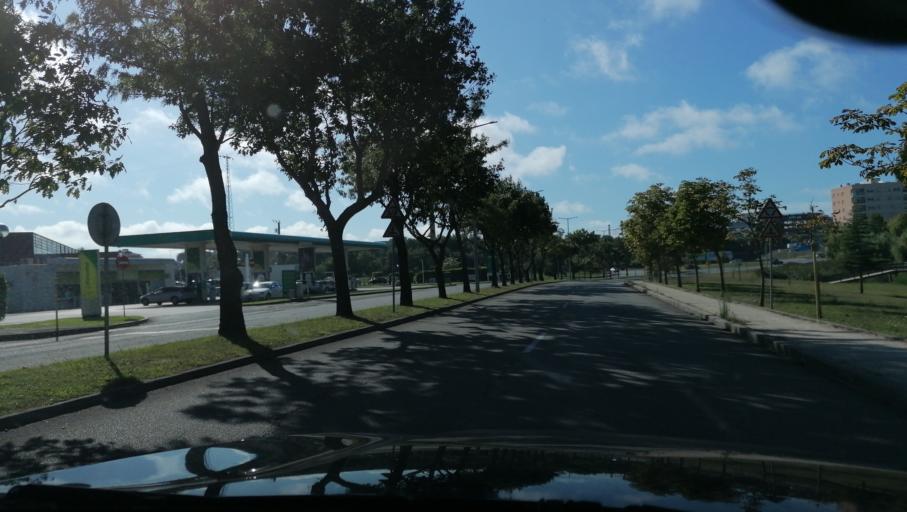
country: PT
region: Aveiro
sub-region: Aveiro
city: Aveiro
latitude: 40.6374
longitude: -8.6389
